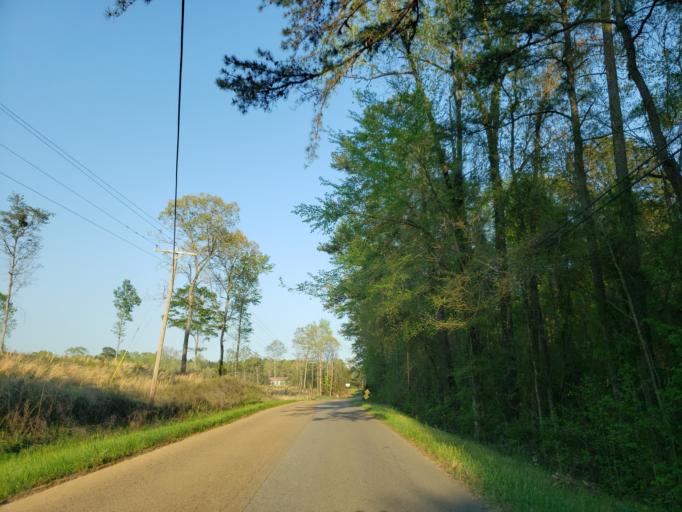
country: US
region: Mississippi
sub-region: Lauderdale County
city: Marion
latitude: 32.3989
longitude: -88.5882
